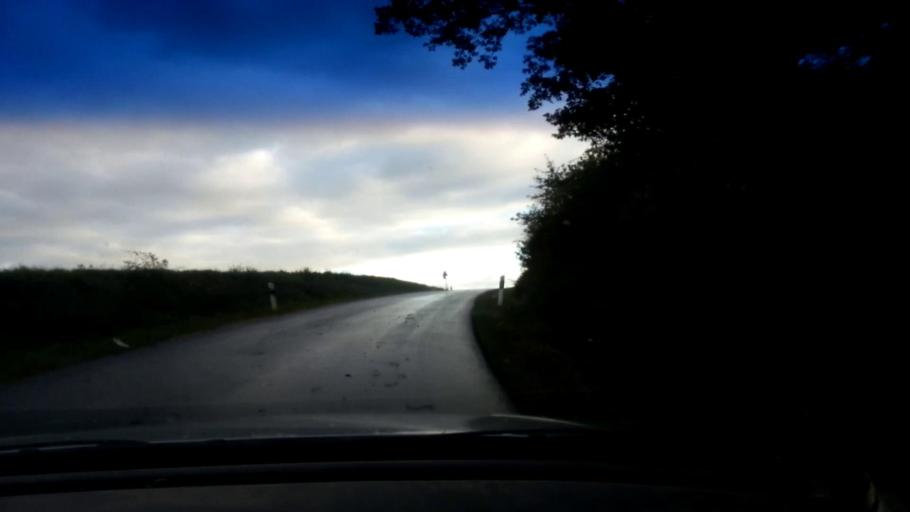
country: DE
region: Bavaria
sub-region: Upper Franconia
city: Burgwindheim
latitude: 49.8138
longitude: 10.6543
